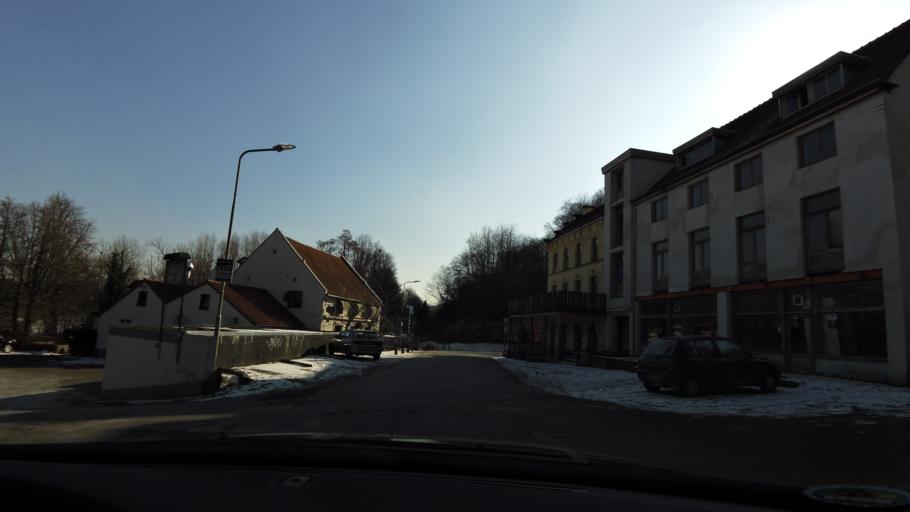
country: NL
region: Limburg
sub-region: Valkenburg aan de Geul
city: Berg
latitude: 50.8690
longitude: 5.7830
